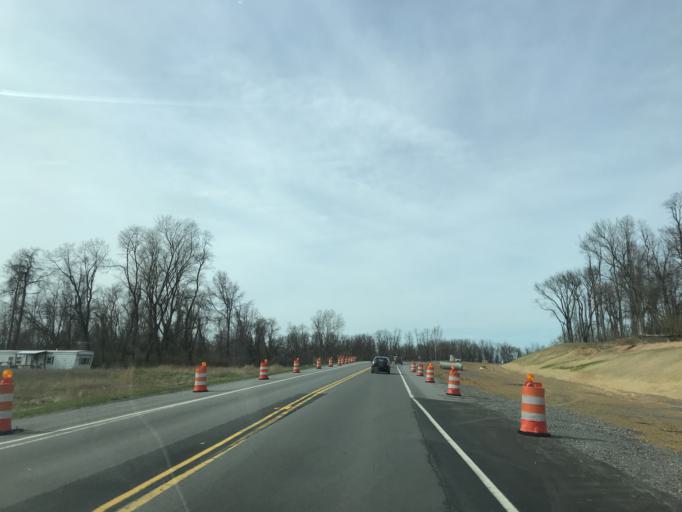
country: US
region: Pennsylvania
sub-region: Union County
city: Lewisburg
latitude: 40.9452
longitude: -76.8531
